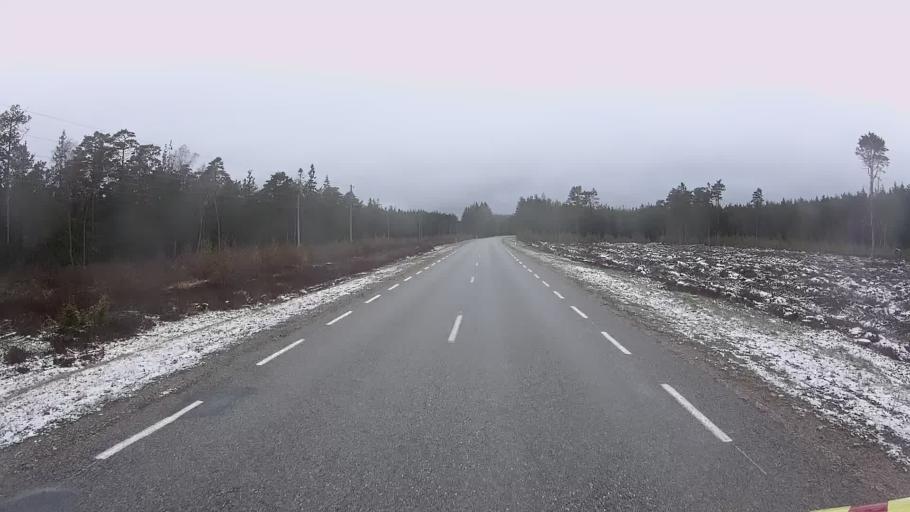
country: EE
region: Hiiumaa
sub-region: Kaerdla linn
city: Kardla
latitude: 59.0247
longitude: 22.6721
